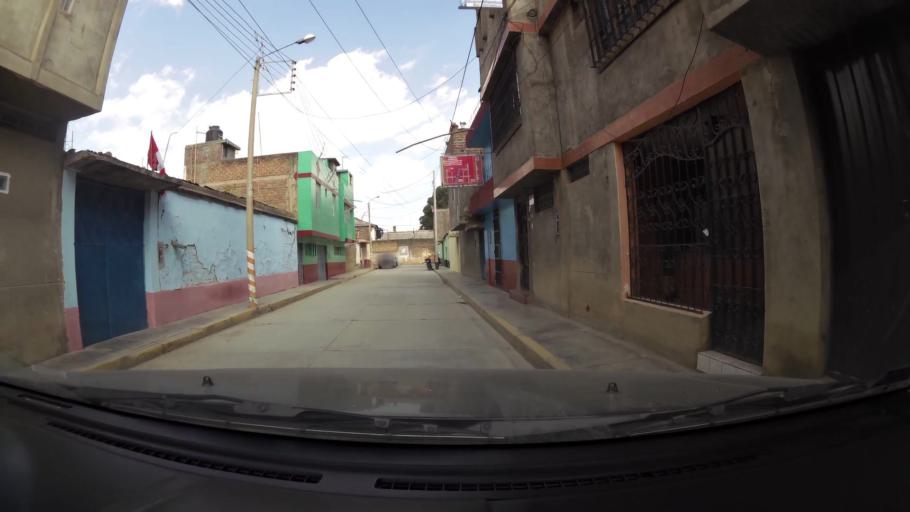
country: PE
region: Junin
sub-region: Provincia de Huancayo
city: Huancayo
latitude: -12.0803
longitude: -75.2014
